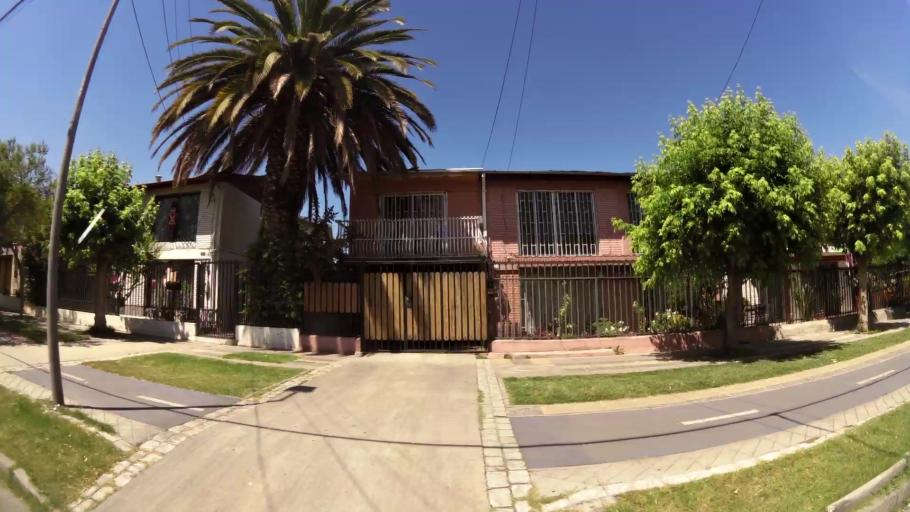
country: CL
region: Santiago Metropolitan
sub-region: Provincia de Maipo
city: San Bernardo
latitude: -33.5684
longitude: -70.6827
